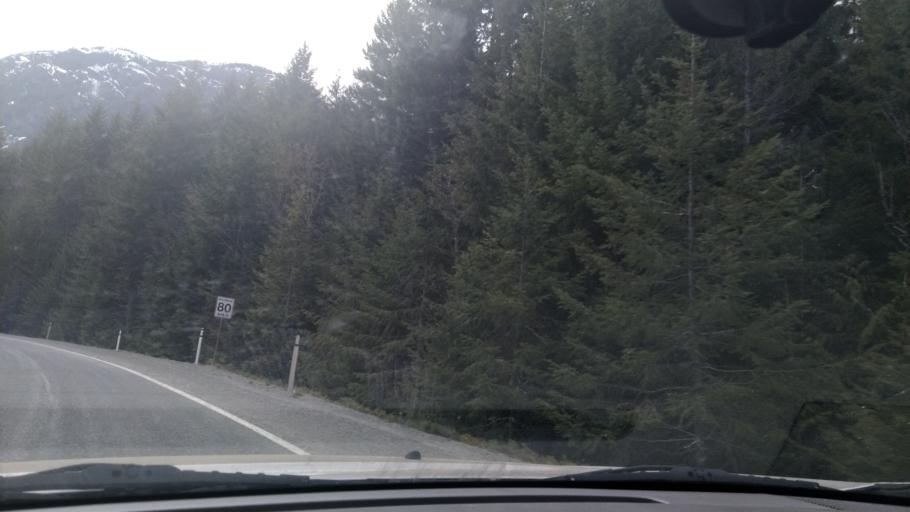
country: CA
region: British Columbia
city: Campbell River
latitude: 49.8371
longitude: -125.6348
